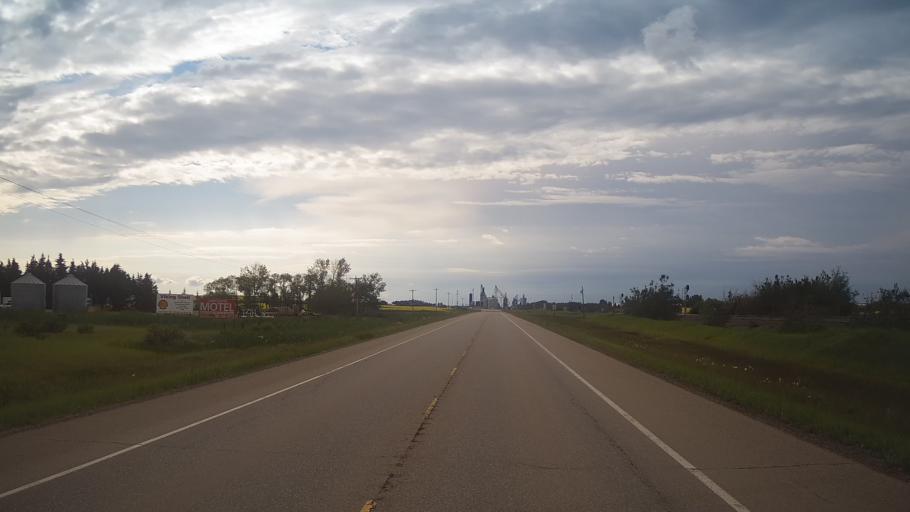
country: CA
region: Alberta
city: Viking
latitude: 53.0847
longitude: -111.7531
